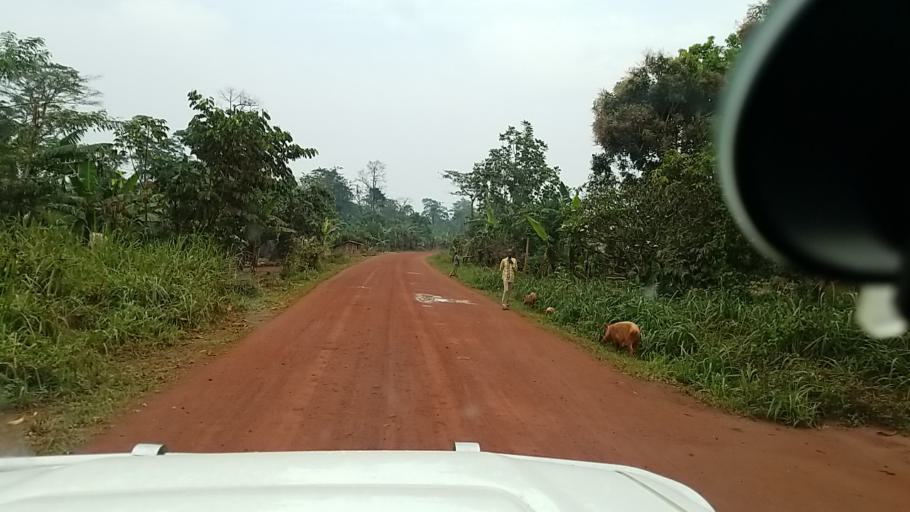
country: CD
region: Equateur
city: Gemena
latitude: 3.1108
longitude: 19.8286
